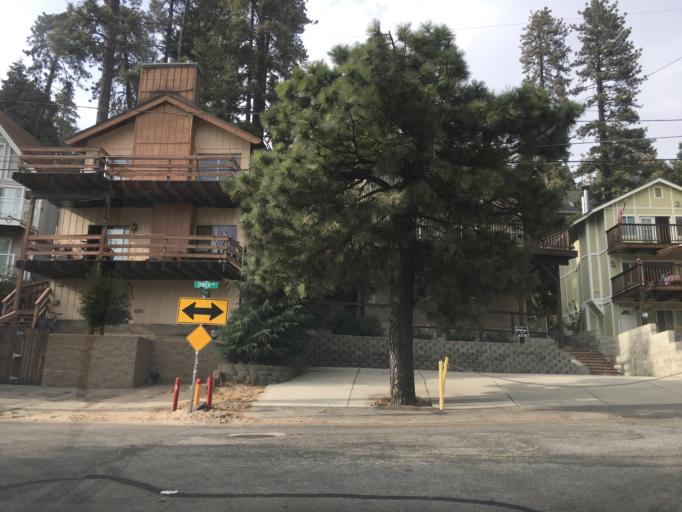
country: US
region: California
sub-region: San Bernardino County
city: Crestline
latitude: 34.2439
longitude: -117.2759
